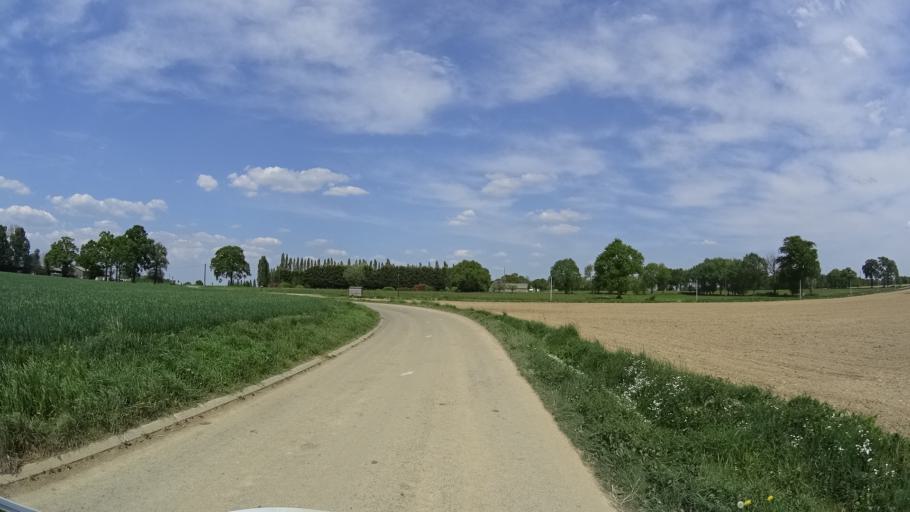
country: FR
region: Brittany
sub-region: Departement d'Ille-et-Vilaine
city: Torce
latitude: 48.0440
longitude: -1.2643
